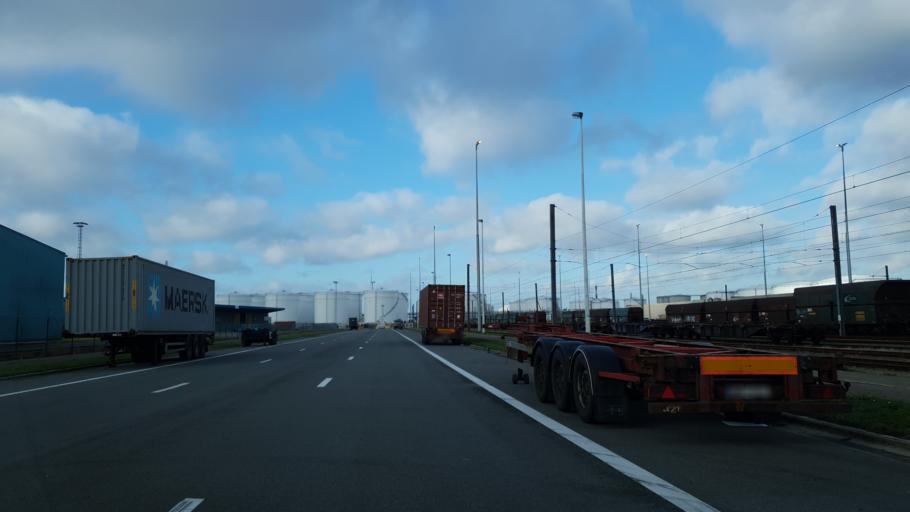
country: BE
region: Flanders
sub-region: Provincie Antwerpen
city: Zwijndrecht
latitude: 51.2672
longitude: 4.3538
